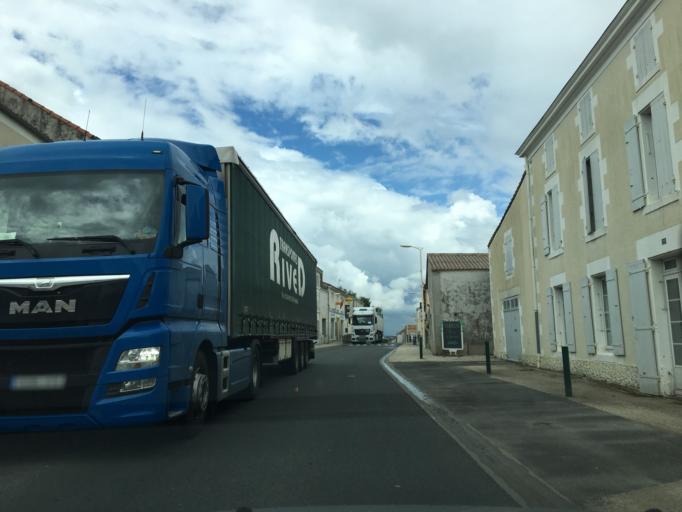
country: FR
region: Poitou-Charentes
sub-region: Departement de la Charente-Maritime
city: Saint-Jean-d'Angely
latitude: 46.0464
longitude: -0.5129
